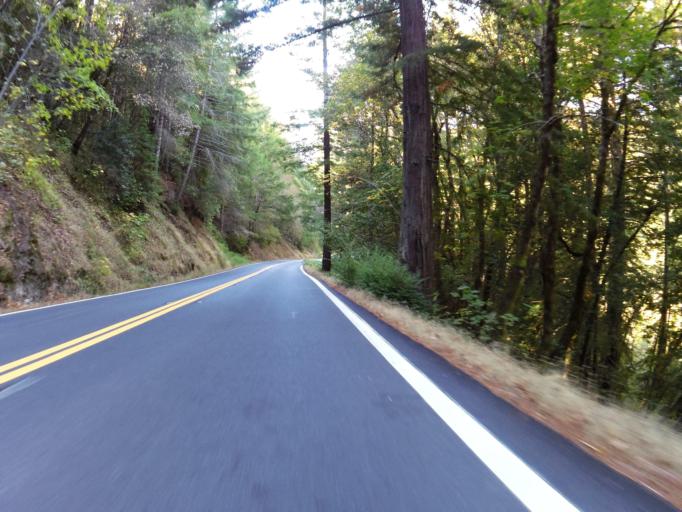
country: US
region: California
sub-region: Humboldt County
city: Redway
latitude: 39.8653
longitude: -123.7197
